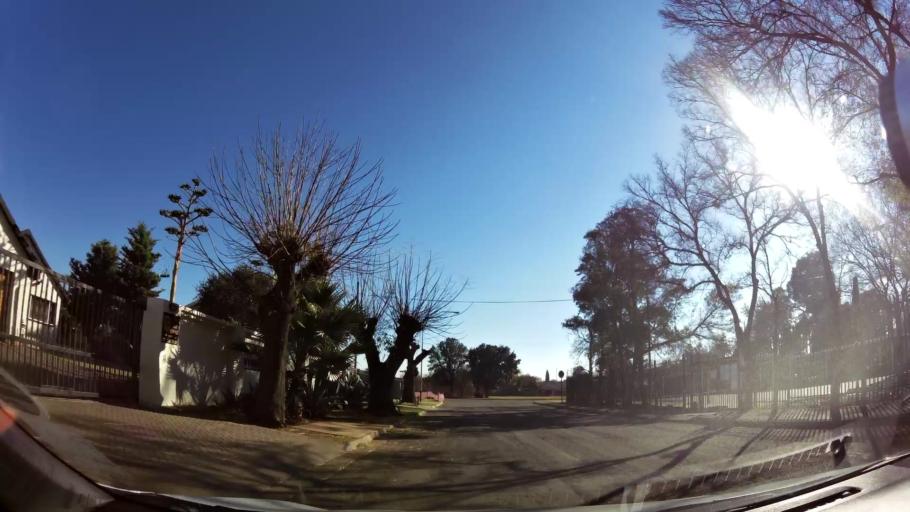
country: ZA
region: Gauteng
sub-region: Ekurhuleni Metropolitan Municipality
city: Germiston
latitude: -26.2821
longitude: 28.1137
